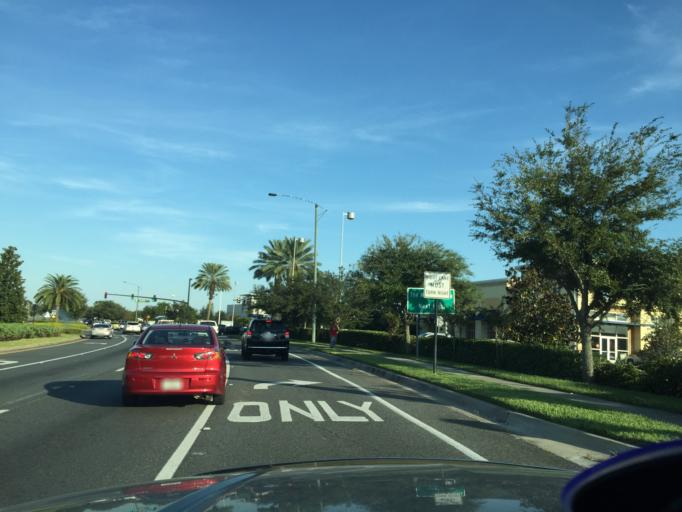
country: US
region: Florida
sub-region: Orange County
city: Oak Ridge
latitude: 28.4868
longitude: -81.4277
